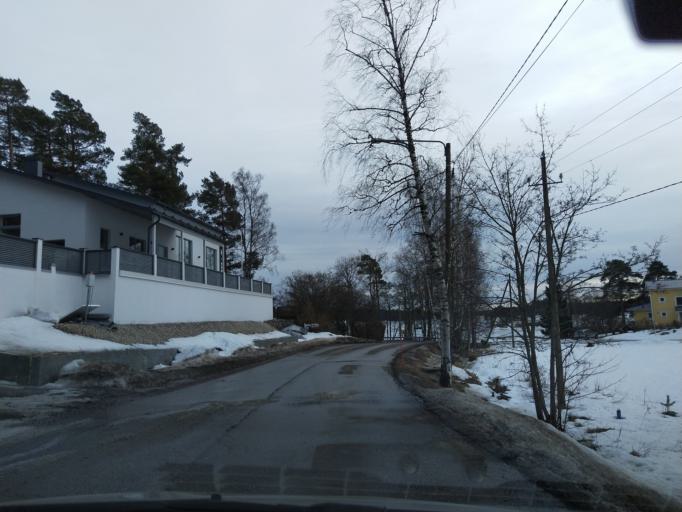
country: FI
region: Uusimaa
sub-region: Helsinki
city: Sibbo
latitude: 60.2569
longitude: 25.2914
